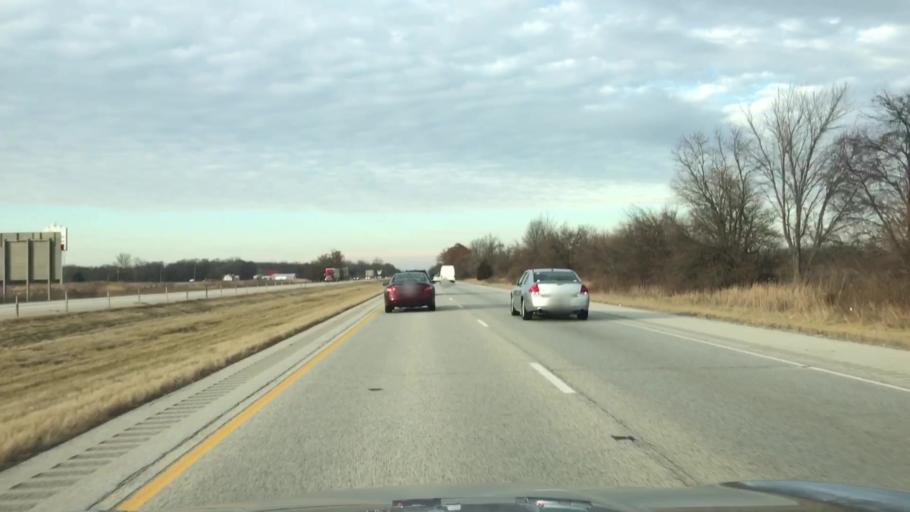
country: US
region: Illinois
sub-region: Sangamon County
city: Grandview
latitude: 39.8485
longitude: -89.5943
